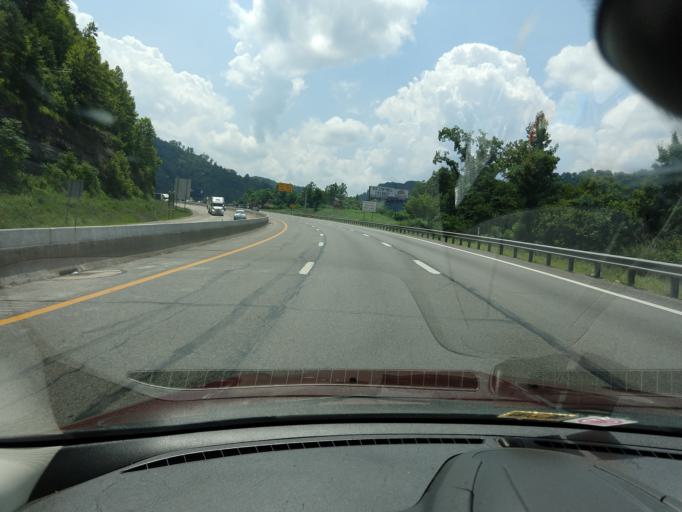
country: US
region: West Virginia
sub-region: Kanawha County
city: Chesapeake
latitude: 38.1896
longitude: -81.4771
